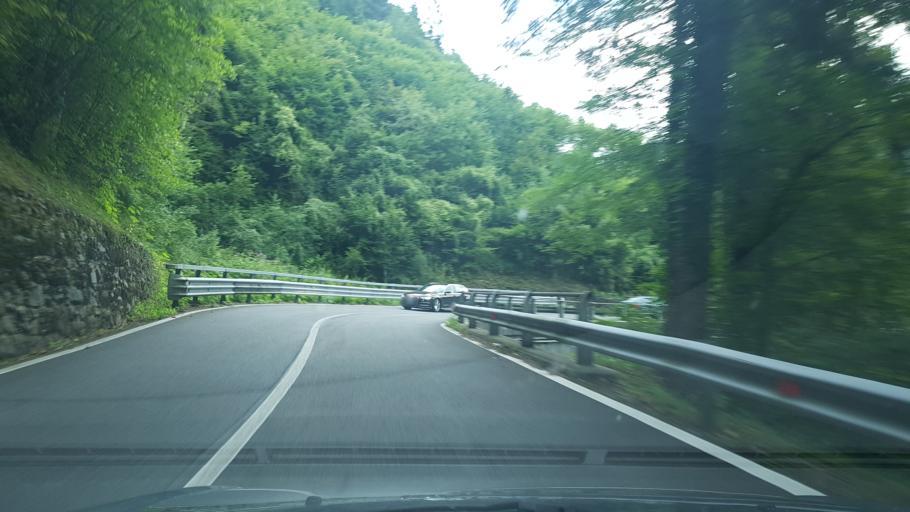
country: IT
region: Friuli Venezia Giulia
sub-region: Provincia di Udine
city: Comeglians
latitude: 46.5263
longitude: 12.8695
